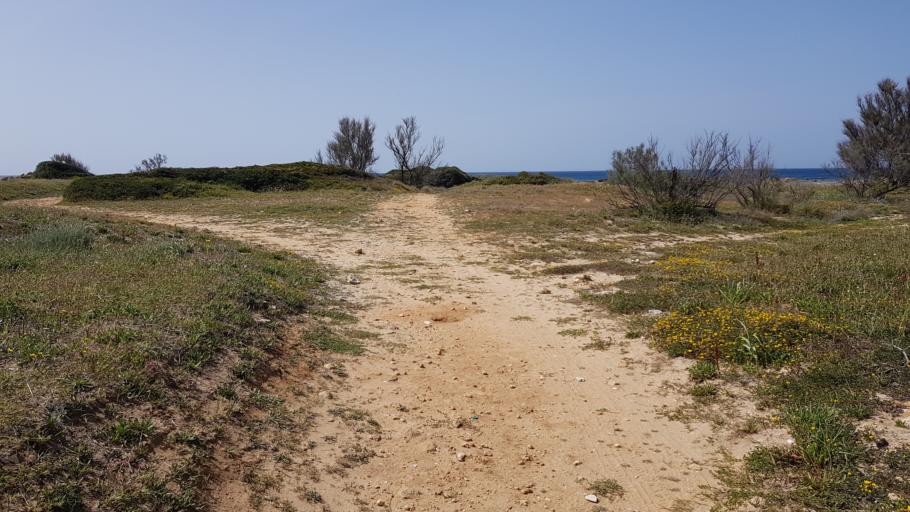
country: IT
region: Apulia
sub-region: Provincia di Brindisi
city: Materdomini
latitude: 40.6836
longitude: 17.9355
